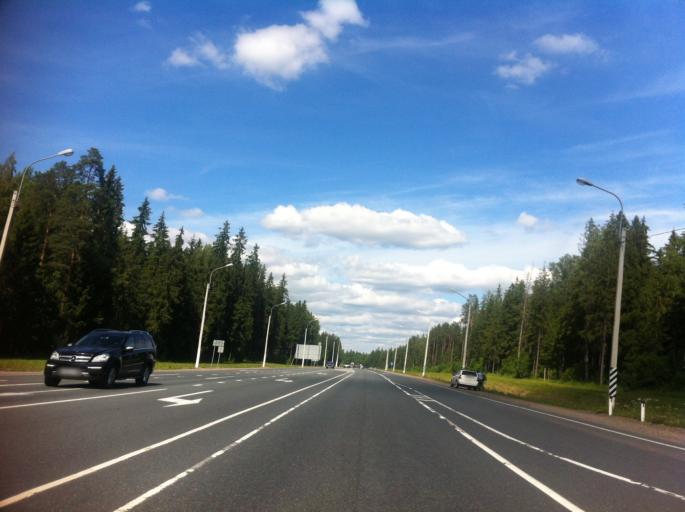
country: RU
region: Leningrad
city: Luga
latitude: 58.6356
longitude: 29.8450
